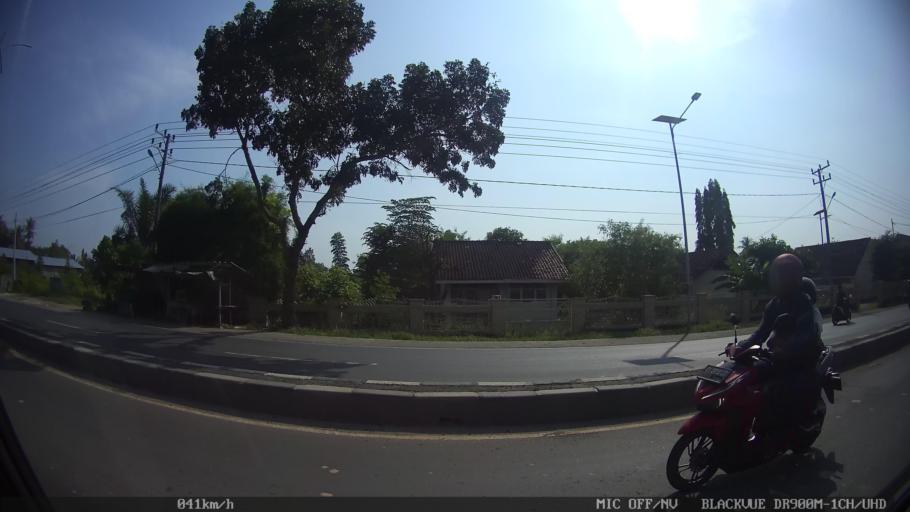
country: ID
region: Lampung
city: Natar
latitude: -5.2479
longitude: 105.1796
